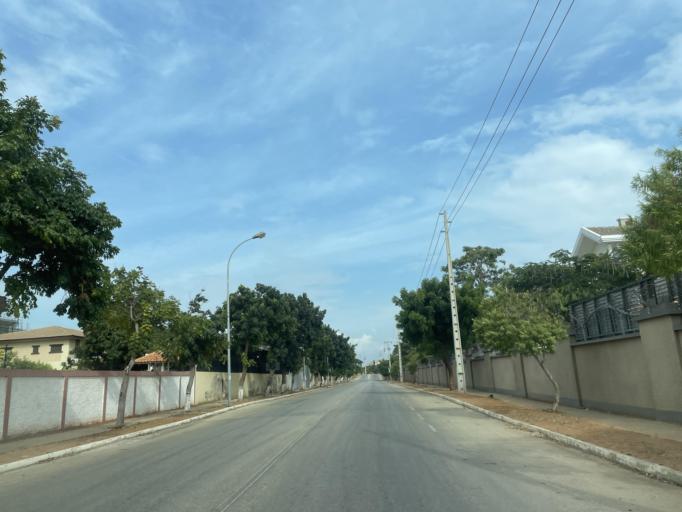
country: AO
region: Luanda
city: Luanda
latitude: -8.9309
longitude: 13.1813
